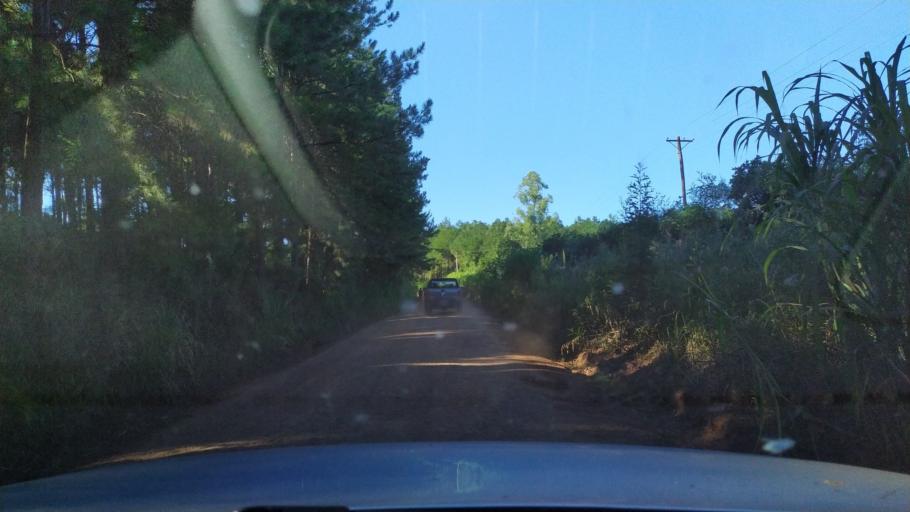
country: AR
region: Misiones
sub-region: Departamento de Montecarlo
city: Montecarlo
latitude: -26.6104
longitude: -54.6985
